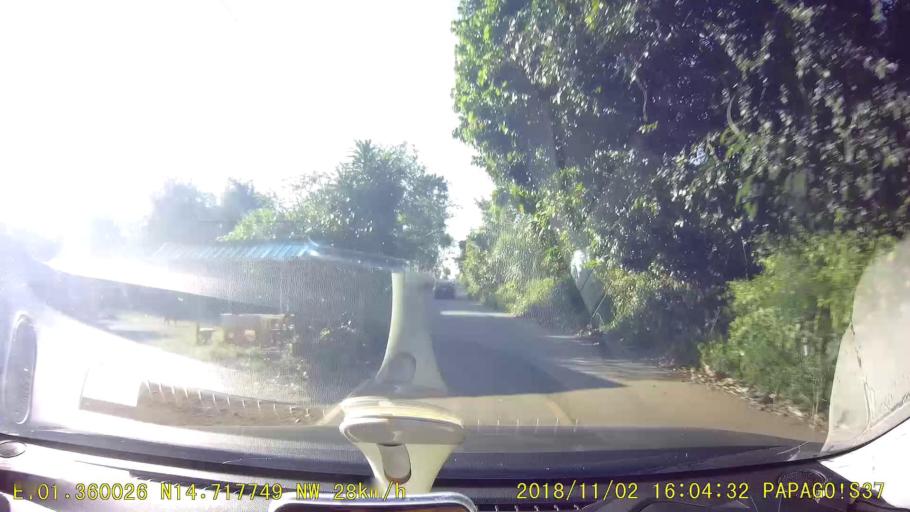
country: TH
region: Nakhon Ratchasima
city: Pak Chong
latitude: 14.7179
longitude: 101.3598
